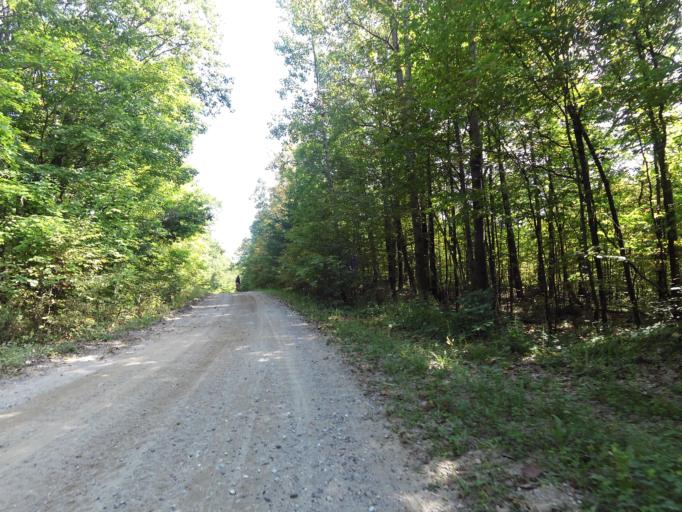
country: CA
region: Ontario
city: Perth
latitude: 45.0184
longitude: -76.6079
